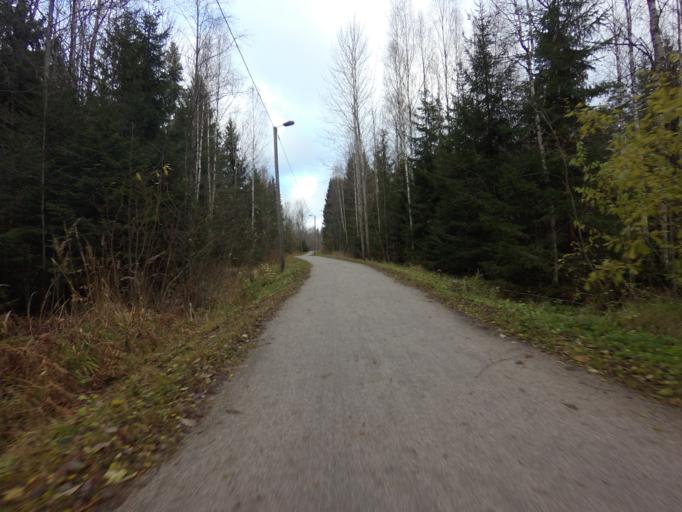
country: FI
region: Uusimaa
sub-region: Helsinki
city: Kauniainen
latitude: 60.1948
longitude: 24.6986
